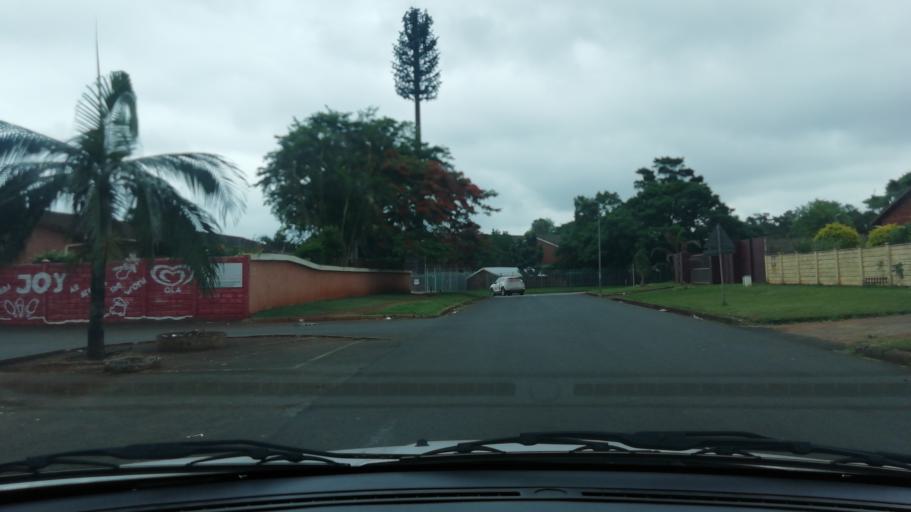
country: ZA
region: KwaZulu-Natal
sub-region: uThungulu District Municipality
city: Empangeni
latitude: -28.7665
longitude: 31.8977
